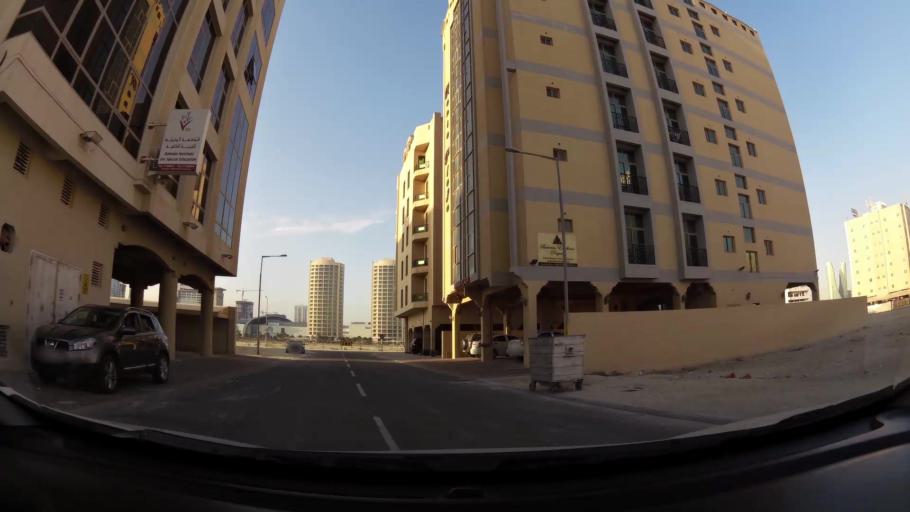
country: BH
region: Manama
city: Jidd Hafs
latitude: 26.2270
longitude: 50.5559
